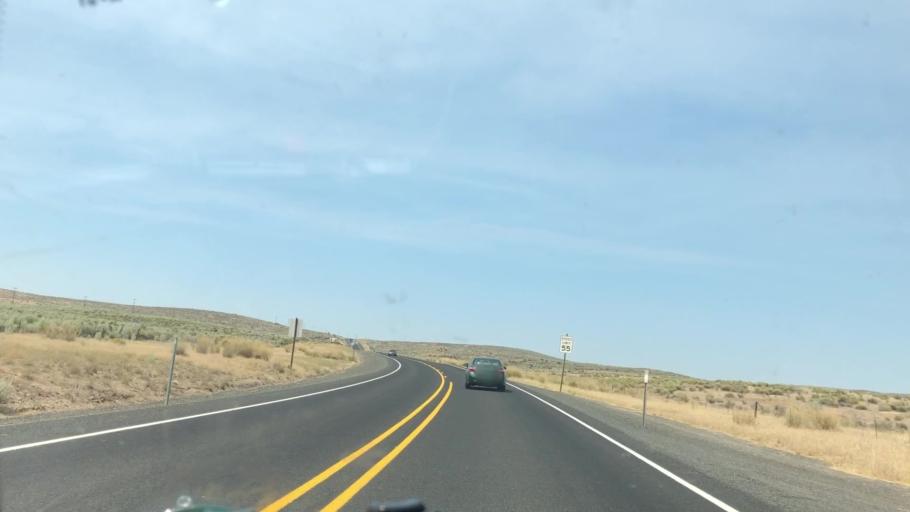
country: US
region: Idaho
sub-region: Owyhee County
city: Murphy
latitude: 42.9829
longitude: -117.0530
